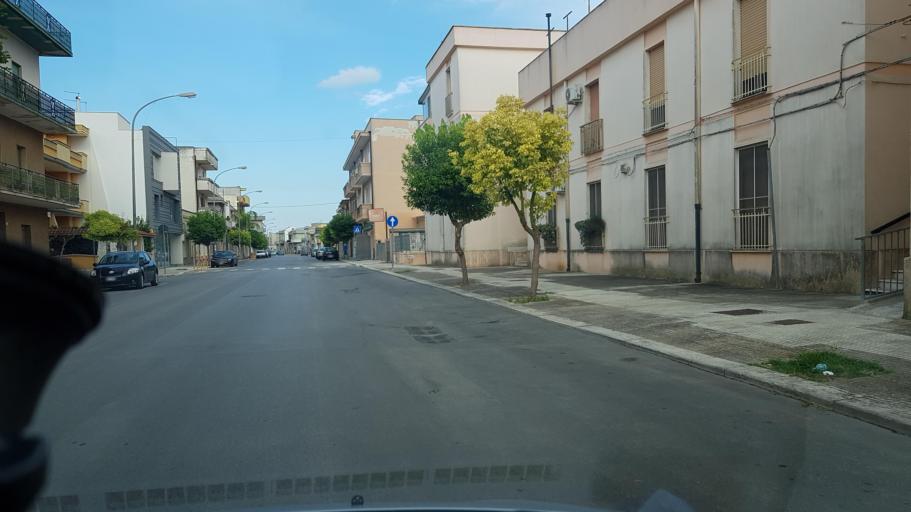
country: IT
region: Apulia
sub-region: Provincia di Brindisi
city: Latiano
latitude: 40.5496
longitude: 17.7112
